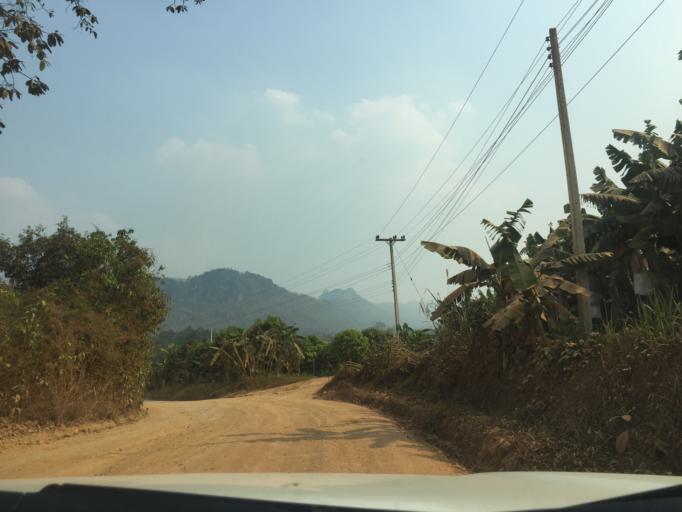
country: LA
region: Xiagnabouli
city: Sainyabuli
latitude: 19.2116
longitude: 101.6939
